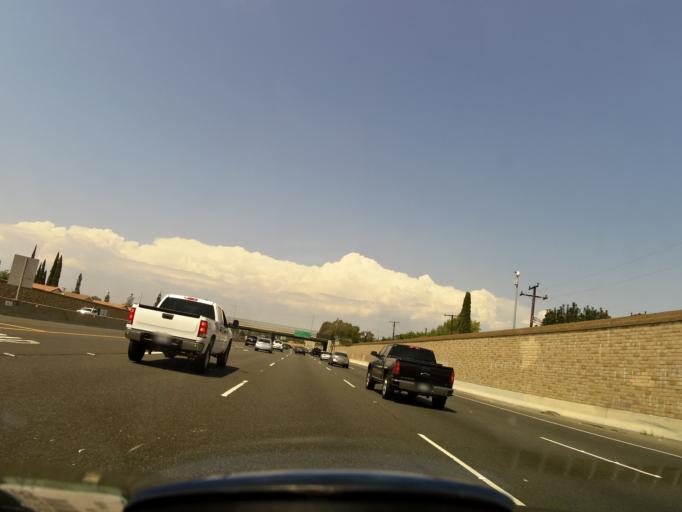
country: US
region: California
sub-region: Orange County
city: Villa Park
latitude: 33.8207
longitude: -117.8319
